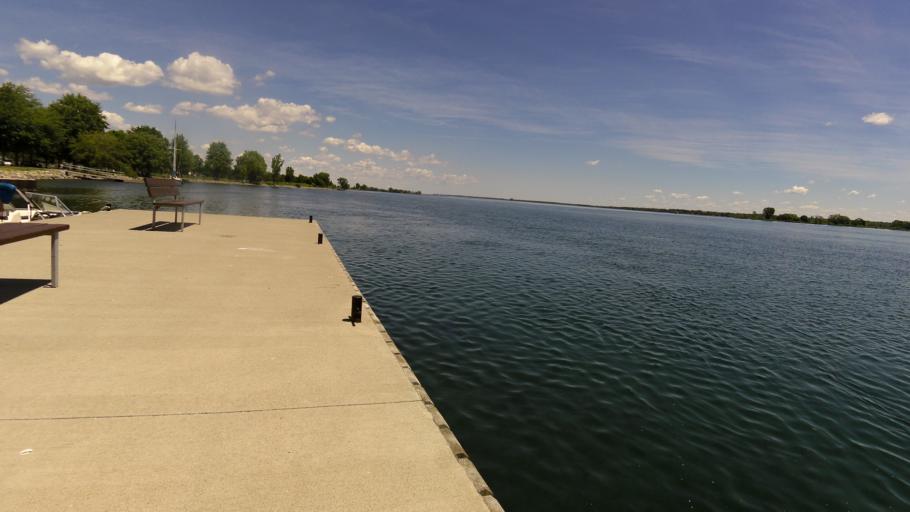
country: US
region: New York
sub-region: St. Lawrence County
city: Norfolk
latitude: 44.8937
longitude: -75.1806
